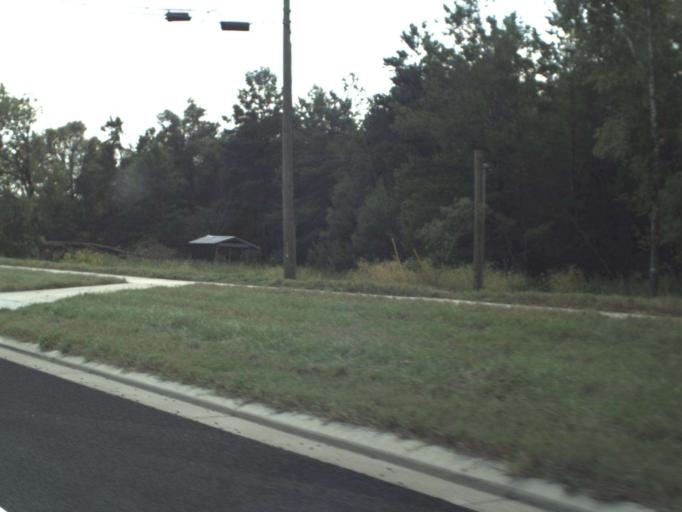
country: US
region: Florida
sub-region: Holmes County
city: Bonifay
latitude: 30.5736
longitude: -85.8078
